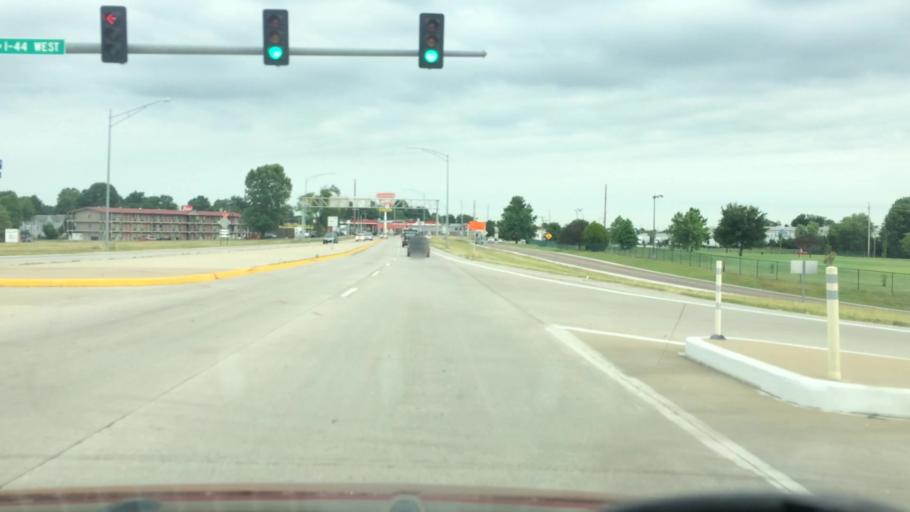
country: US
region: Missouri
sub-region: Greene County
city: Springfield
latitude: 37.2516
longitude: -93.2633
